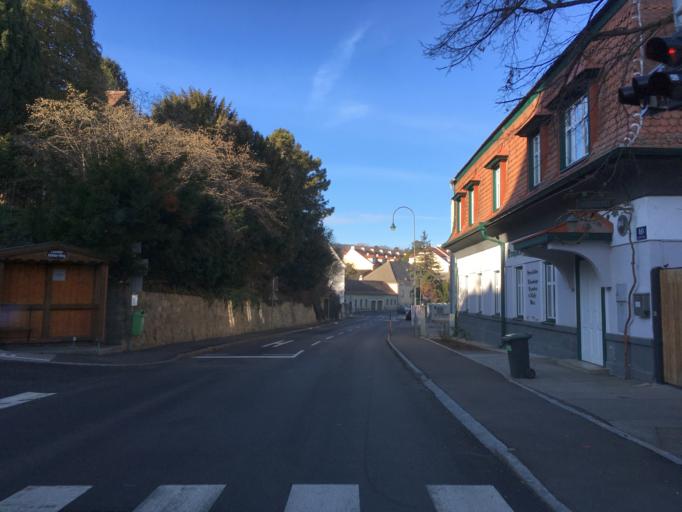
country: AT
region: Lower Austria
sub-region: Politischer Bezirk Wien-Umgebung
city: Klosterneuburg
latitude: 48.3284
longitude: 16.3009
